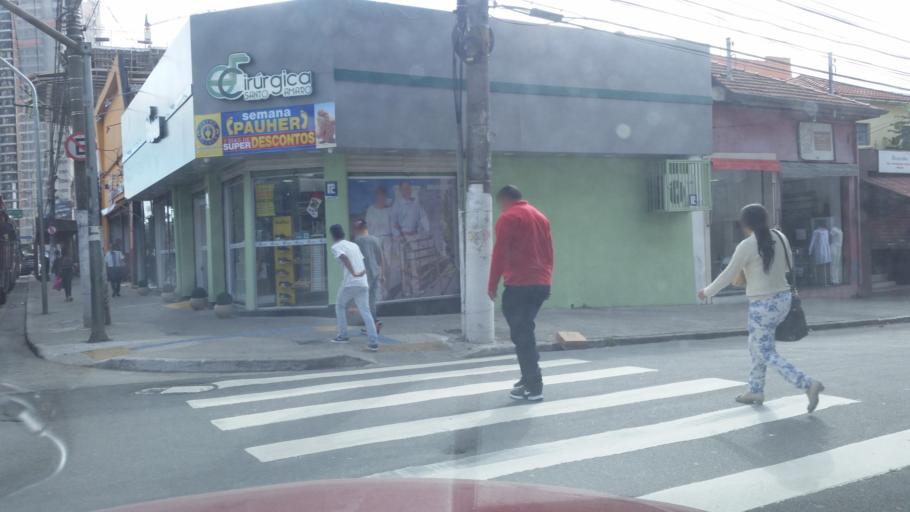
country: BR
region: Sao Paulo
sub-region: Diadema
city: Diadema
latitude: -23.6484
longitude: -46.7044
